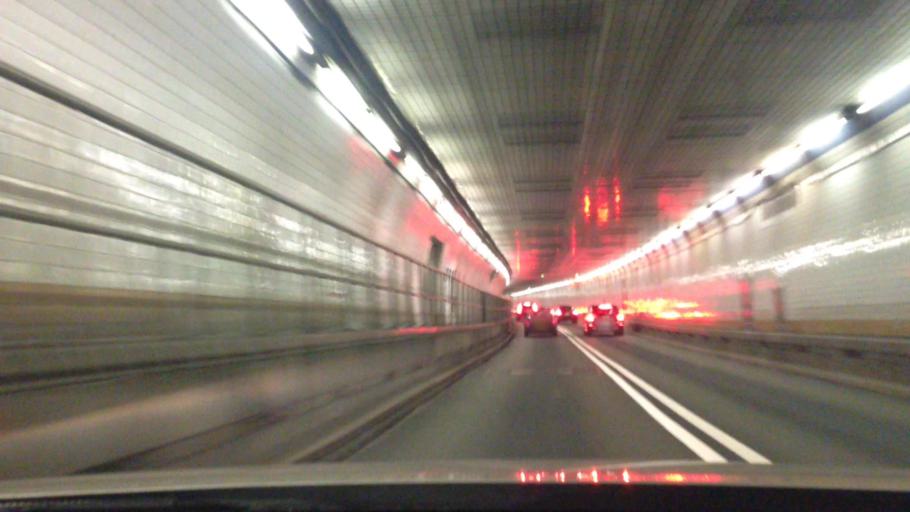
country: US
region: New York
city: New York City
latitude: 40.7259
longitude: -74.0196
